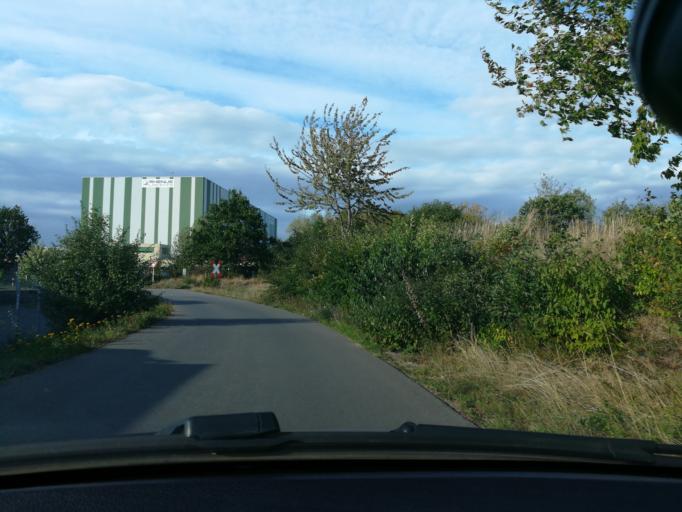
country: DE
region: North Rhine-Westphalia
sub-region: Regierungsbezirk Detmold
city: Minden
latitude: 52.3059
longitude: 8.9585
